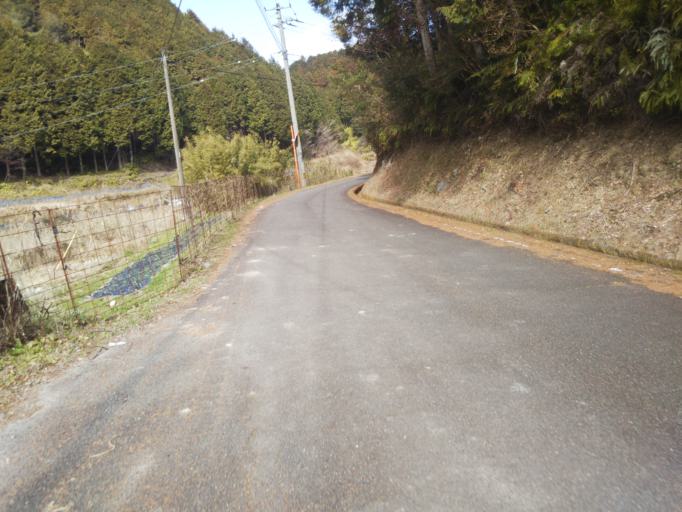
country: JP
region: Kochi
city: Nakamura
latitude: 33.0377
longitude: 132.9851
